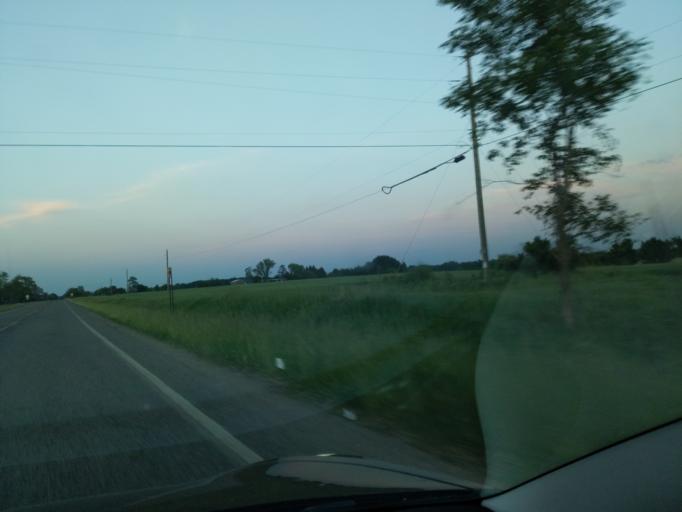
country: US
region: Michigan
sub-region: Barry County
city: Nashville
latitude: 42.5383
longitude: -85.0539
